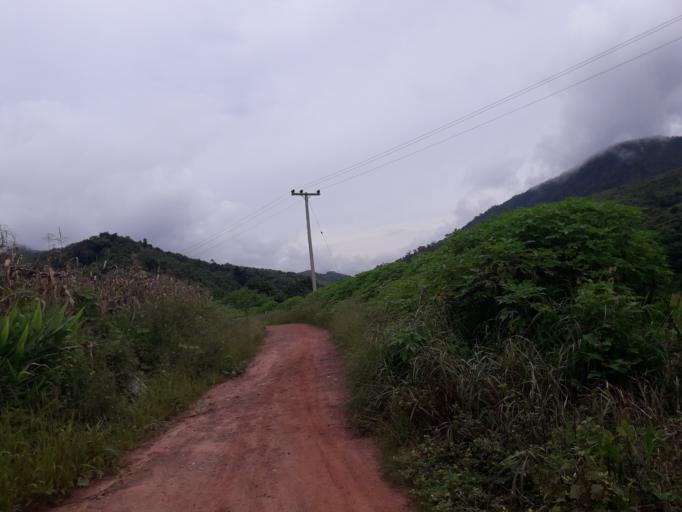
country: CN
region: Yunnan
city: Menglie
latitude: 22.2258
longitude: 101.6376
